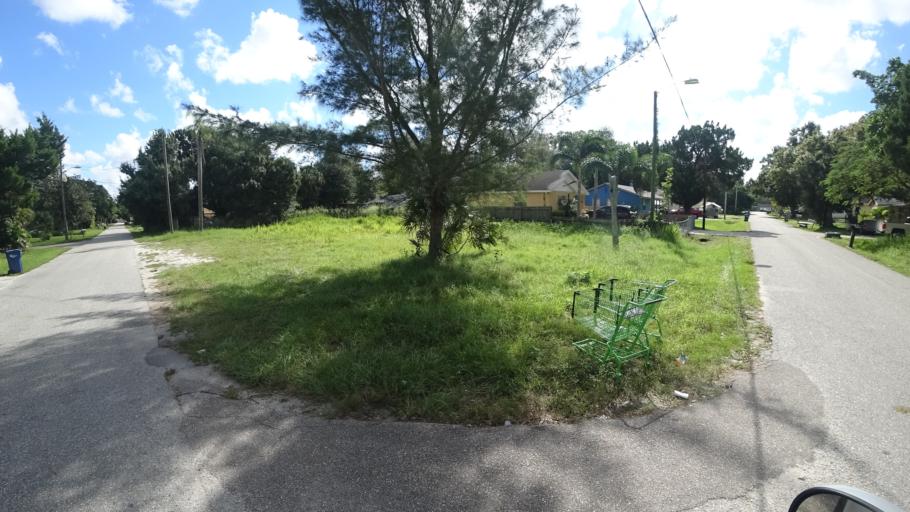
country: US
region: Florida
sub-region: Manatee County
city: West Samoset
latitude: 27.4752
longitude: -82.5579
